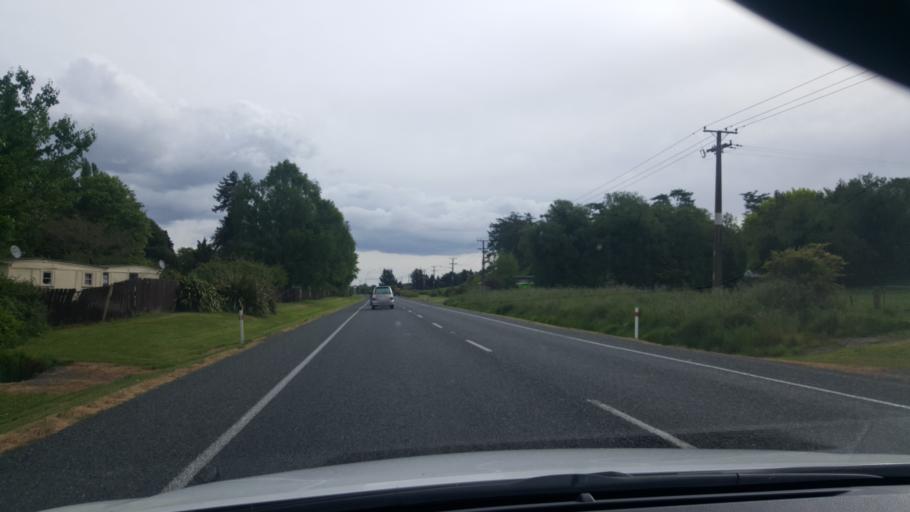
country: NZ
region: Waikato
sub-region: Taupo District
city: Taupo
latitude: -38.4679
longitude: 176.3097
